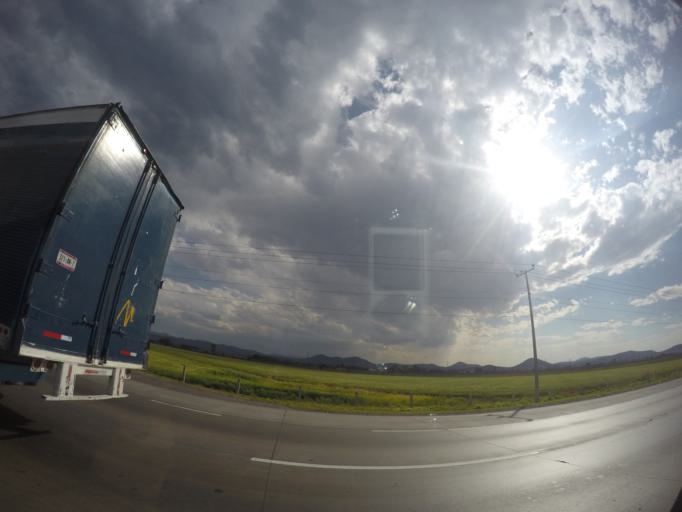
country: MX
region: Queretaro
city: La Estancia
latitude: 20.4531
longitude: -100.0863
